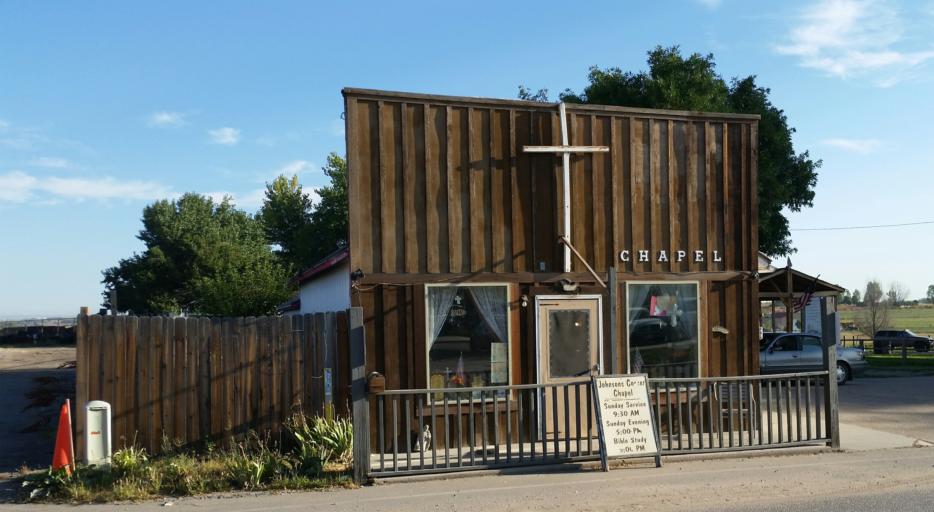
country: US
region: Colorado
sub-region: Weld County
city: Johnstown
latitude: 40.3636
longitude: -104.9839
